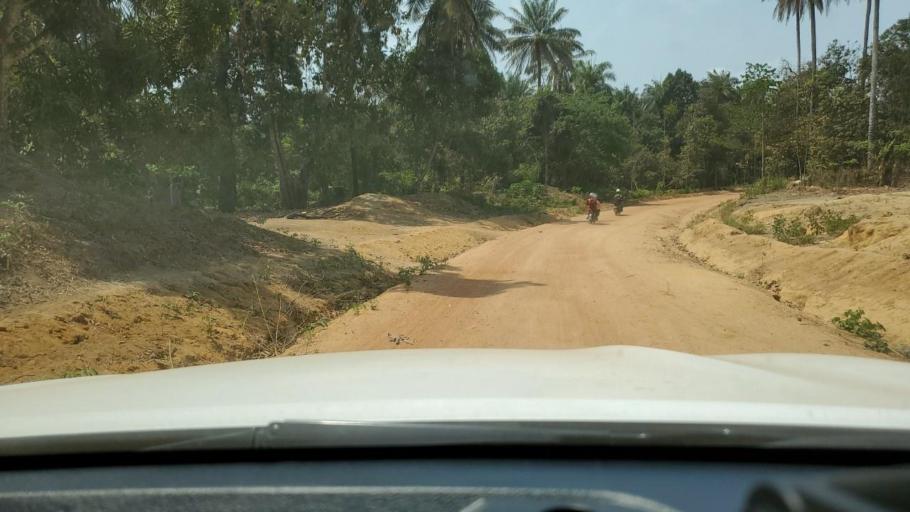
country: GN
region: Boke
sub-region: Boffa
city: Boffa
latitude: 10.0849
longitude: -13.8648
